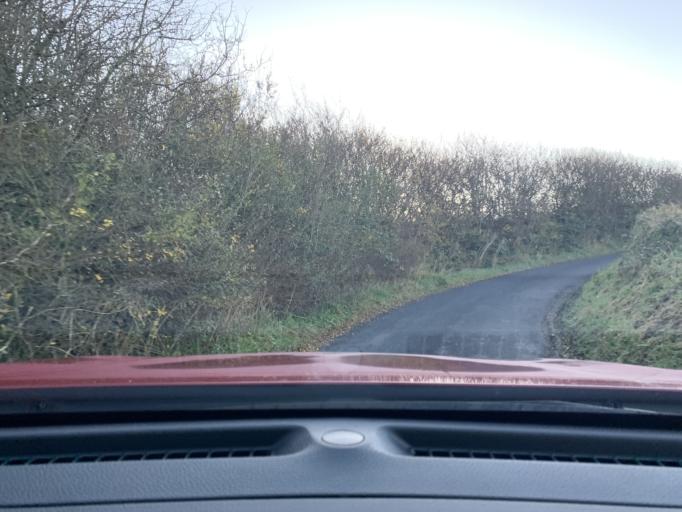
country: IE
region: Connaught
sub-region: Sligo
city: Ballymote
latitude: 54.0668
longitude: -8.5354
